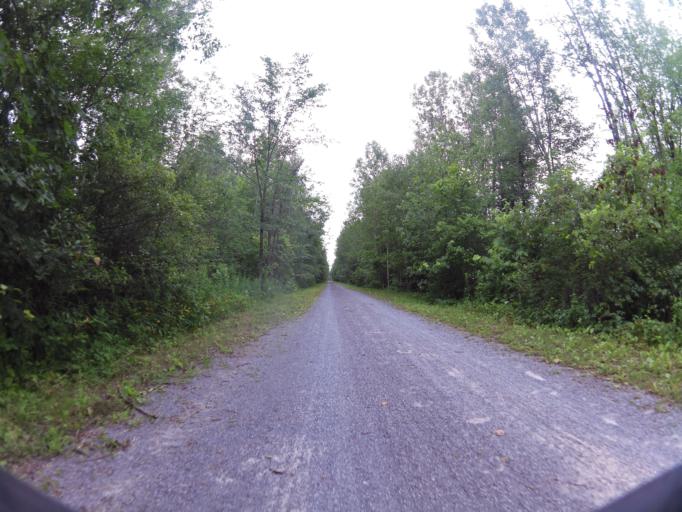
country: CA
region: Ontario
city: Ottawa
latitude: 45.2065
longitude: -75.6248
